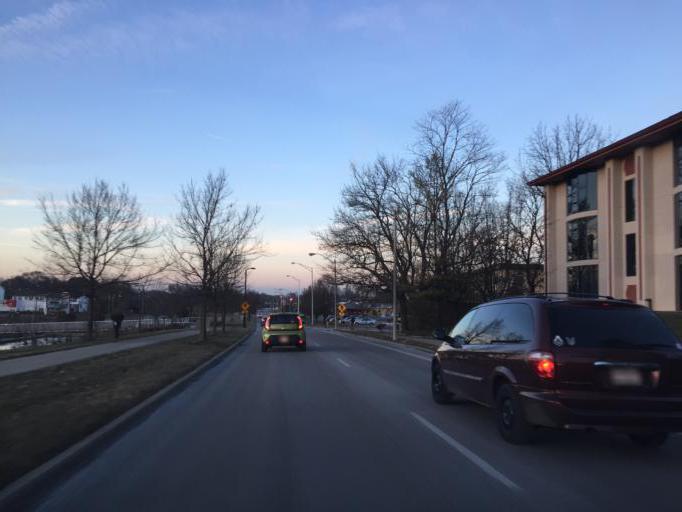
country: US
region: Indiana
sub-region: Monroe County
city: Bloomington
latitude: 39.1807
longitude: -86.5337
